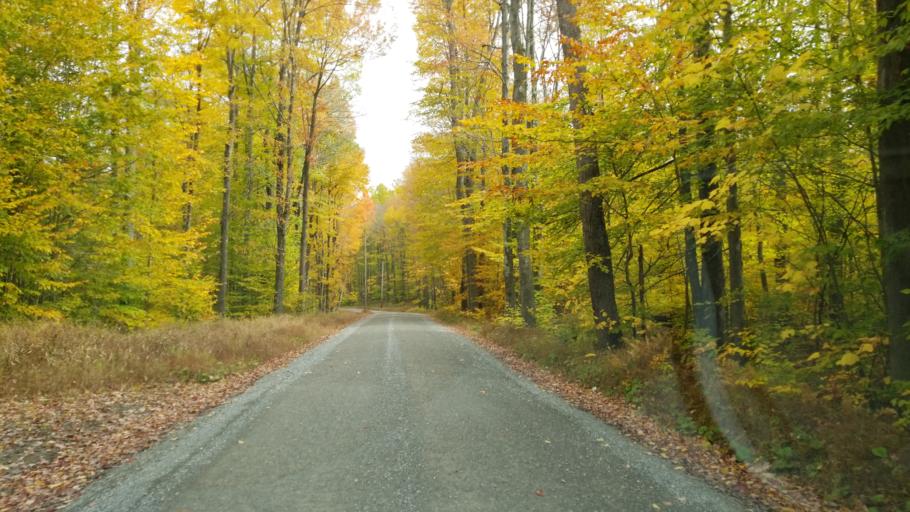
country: US
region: Pennsylvania
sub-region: Clearfield County
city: Clearfield
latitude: 41.1961
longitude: -78.3916
